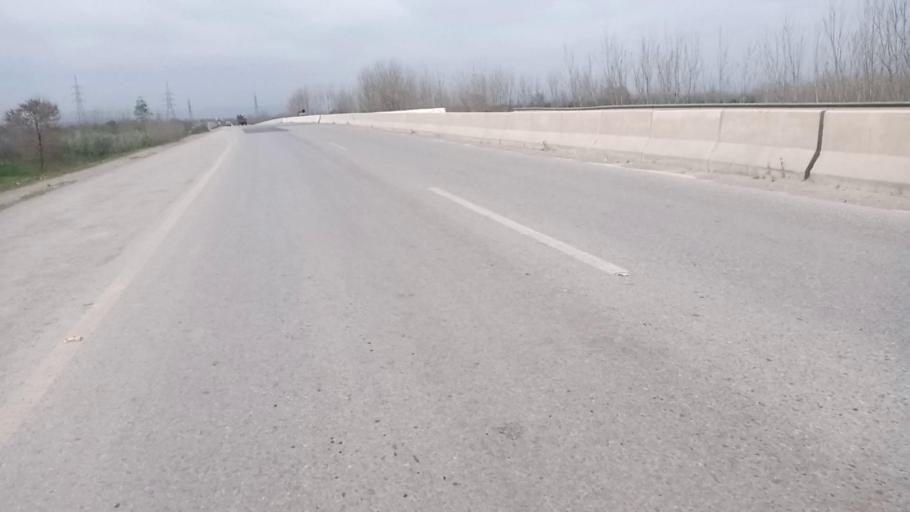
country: PK
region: Khyber Pakhtunkhwa
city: Peshawar
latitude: 34.0597
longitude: 71.6078
